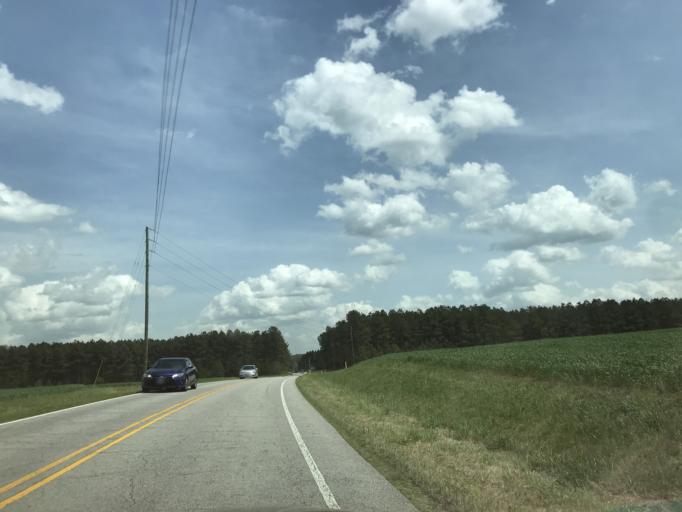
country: US
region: North Carolina
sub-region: Nash County
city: Spring Hope
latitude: 35.9652
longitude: -78.2357
